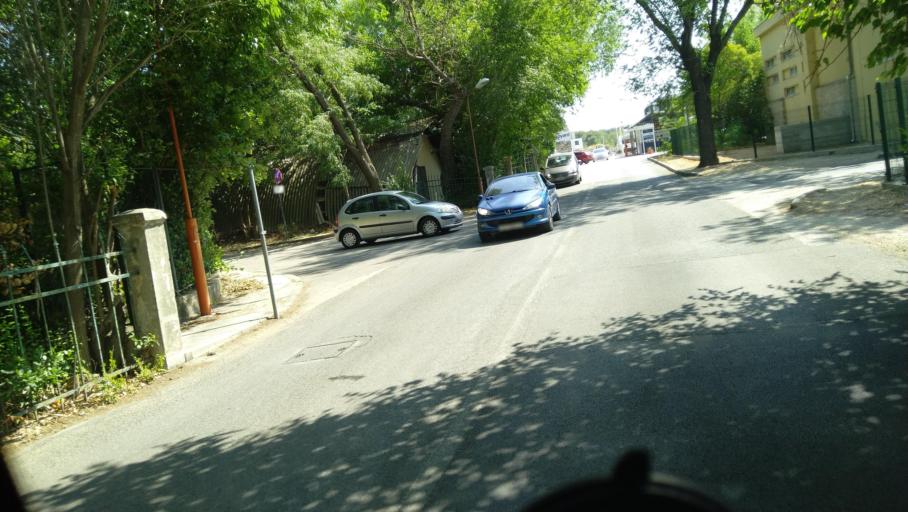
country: HR
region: Sibensko-Kniniska
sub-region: Grad Sibenik
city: Sibenik
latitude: 43.7191
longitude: 15.9063
